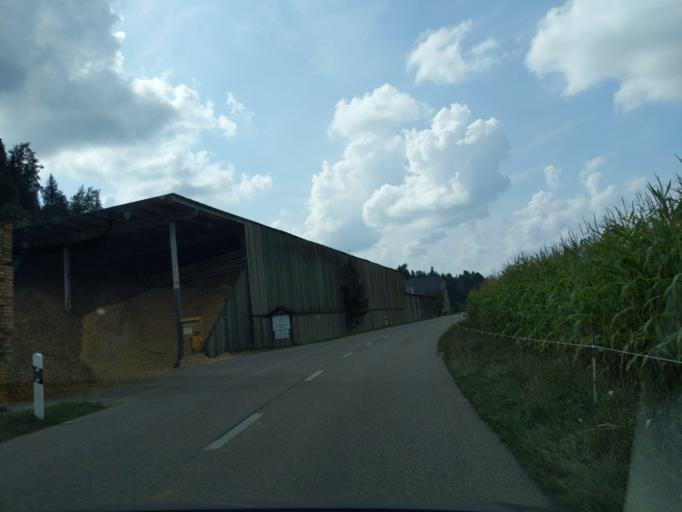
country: CH
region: Bern
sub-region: Oberaargau
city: Wyssachen
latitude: 47.0470
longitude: 7.8234
